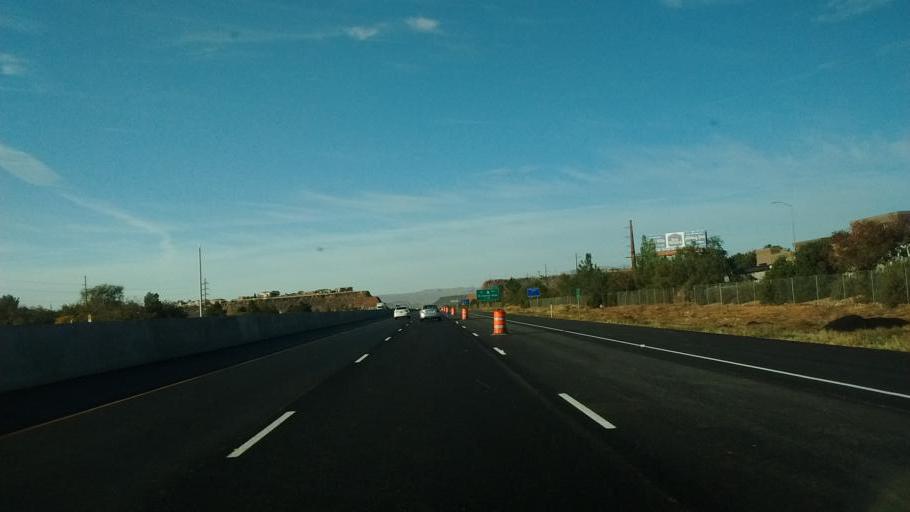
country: US
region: Utah
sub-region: Washington County
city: Washington
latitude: 37.1218
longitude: -113.5387
